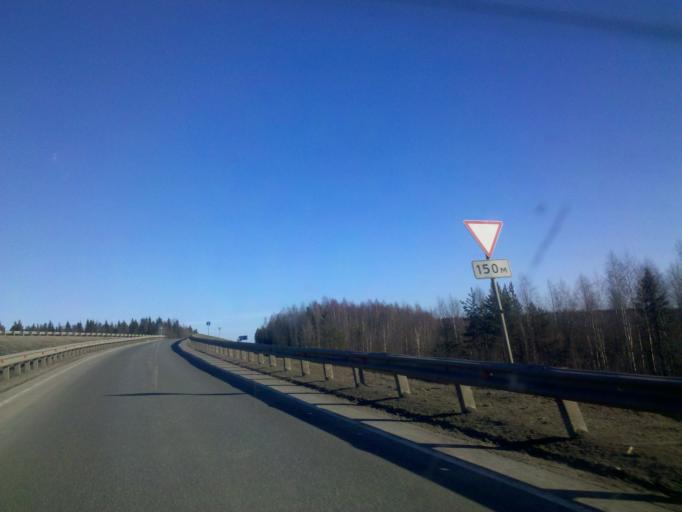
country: RU
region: Republic of Karelia
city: Shuya
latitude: 61.8450
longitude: 34.1975
